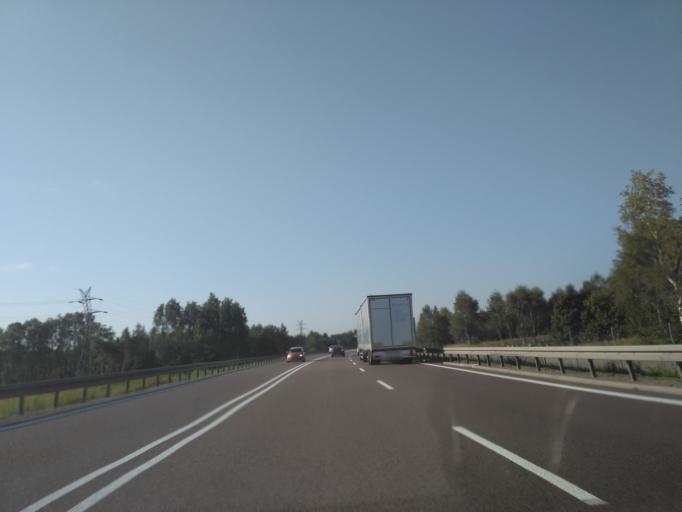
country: PL
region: Subcarpathian Voivodeship
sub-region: Powiat rzeszowski
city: Wolka Podlesna
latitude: 50.1247
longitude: 22.0809
